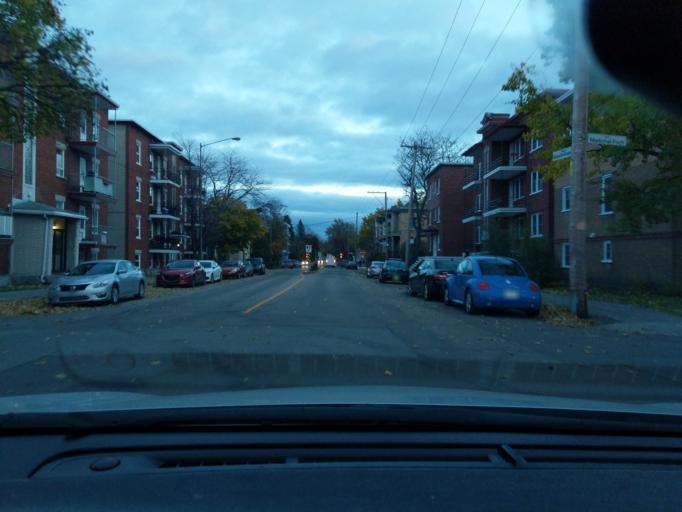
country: CA
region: Quebec
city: Quebec
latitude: 46.7919
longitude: -71.2534
